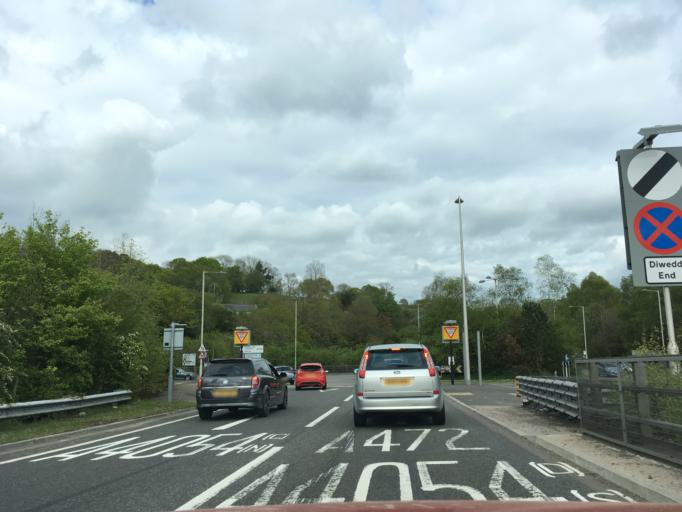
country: GB
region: Wales
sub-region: Merthyr Tydfil County Borough
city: Treharris
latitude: 51.6528
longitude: -3.3119
